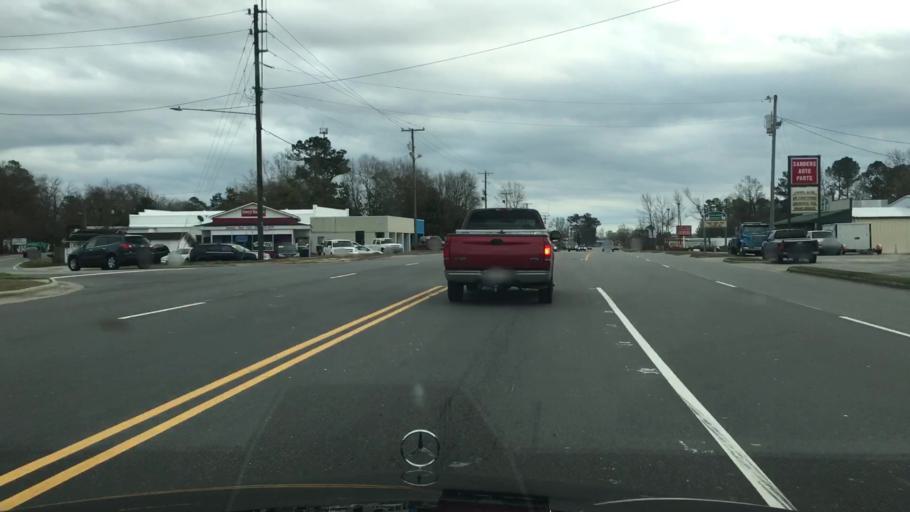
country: US
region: North Carolina
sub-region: Onslow County
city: Richlands
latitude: 34.9024
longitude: -77.5538
